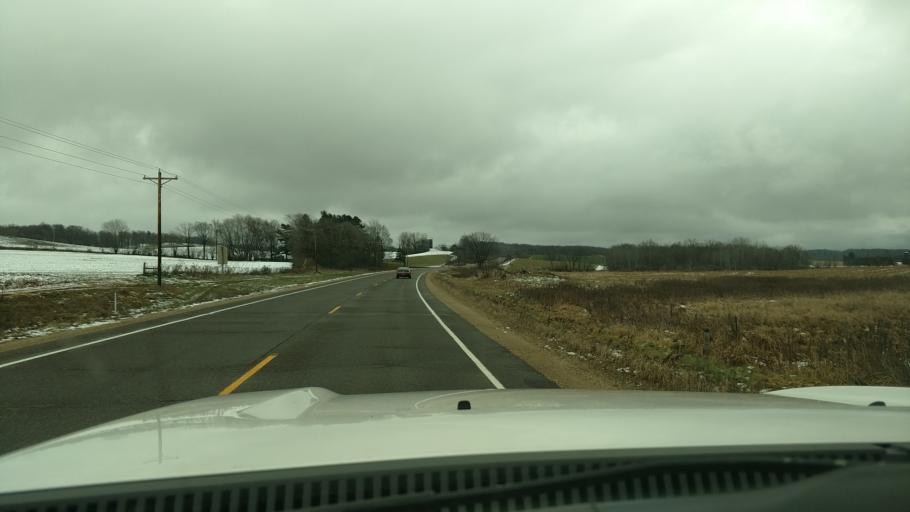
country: US
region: Wisconsin
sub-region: Dunn County
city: Boyceville
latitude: 45.1399
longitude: -91.9667
